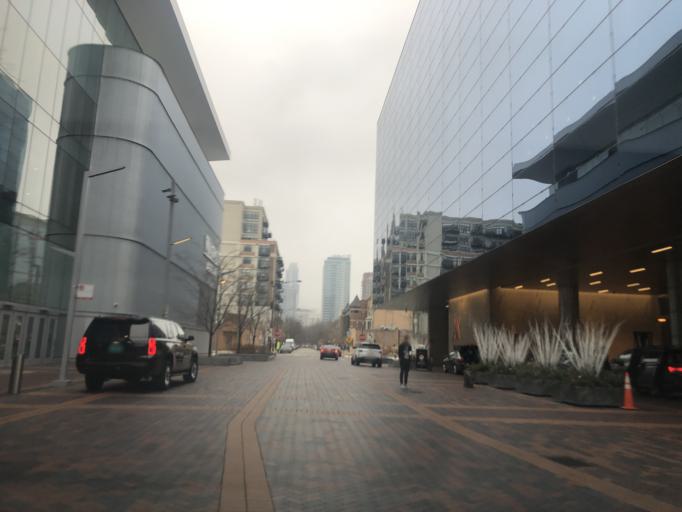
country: US
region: Illinois
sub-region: Cook County
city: Chicago
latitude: 41.8537
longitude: -87.6206
